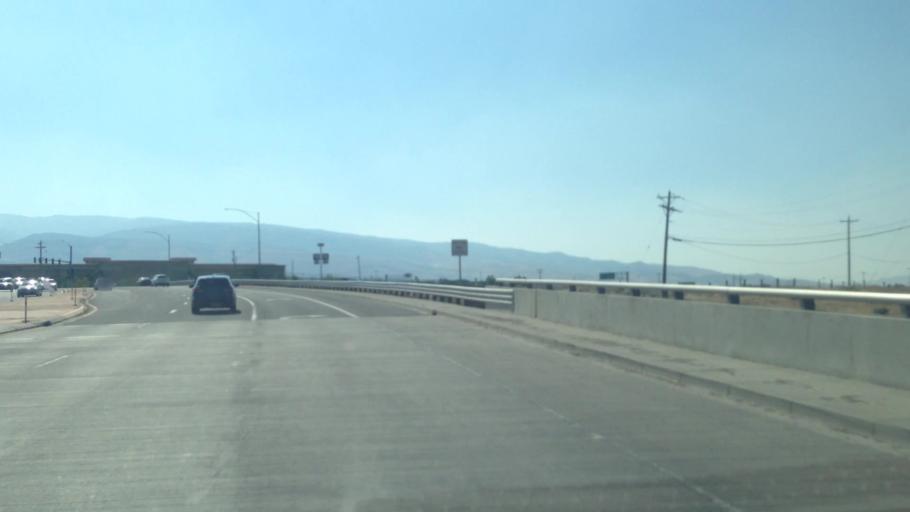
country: US
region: Nevada
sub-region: Washoe County
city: Sparks
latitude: 39.4031
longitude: -119.7435
